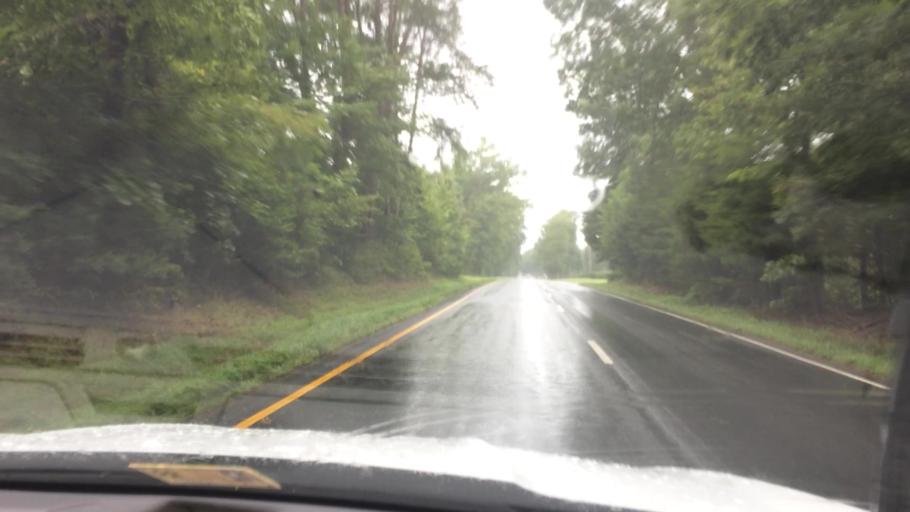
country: US
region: Virginia
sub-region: King William County
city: West Point
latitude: 37.5102
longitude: -76.8497
